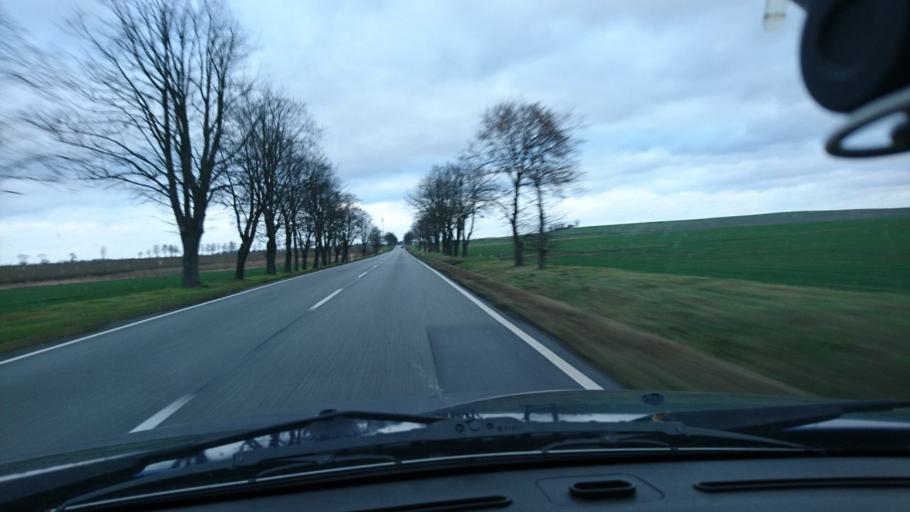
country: PL
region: Opole Voivodeship
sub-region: Powiat kluczborski
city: Byczyna
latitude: 51.0891
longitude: 18.2002
